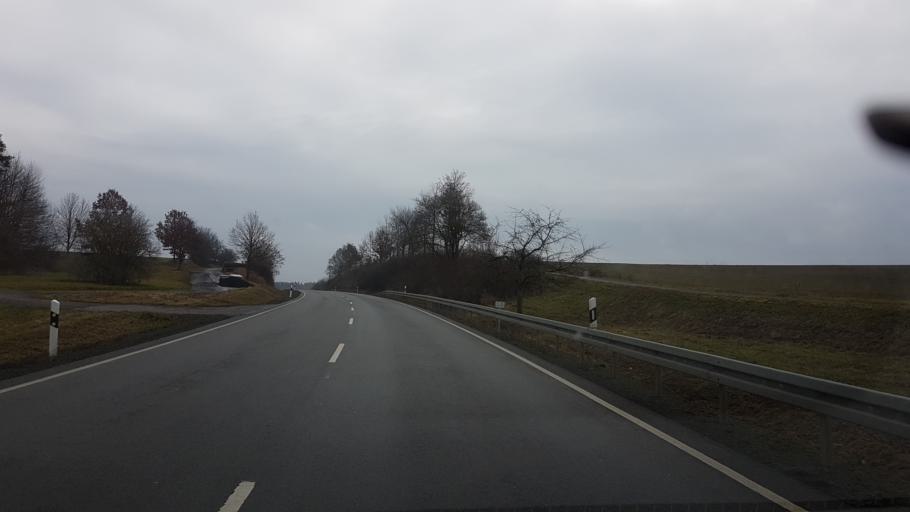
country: DE
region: Bavaria
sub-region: Regierungsbezirk Unterfranken
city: Bundorf
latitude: 50.2619
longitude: 10.5414
